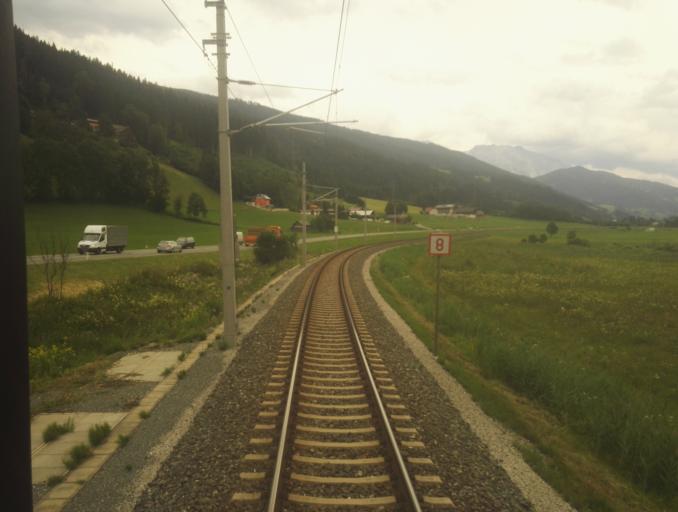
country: AT
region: Salzburg
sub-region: Politischer Bezirk Sankt Johann im Pongau
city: Forstau
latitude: 47.3887
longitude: 13.4962
